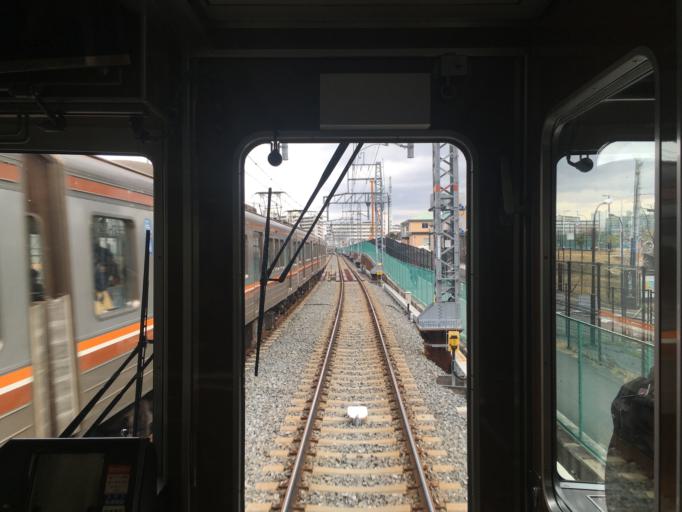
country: JP
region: Osaka
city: Suita
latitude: 34.7319
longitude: 135.5143
